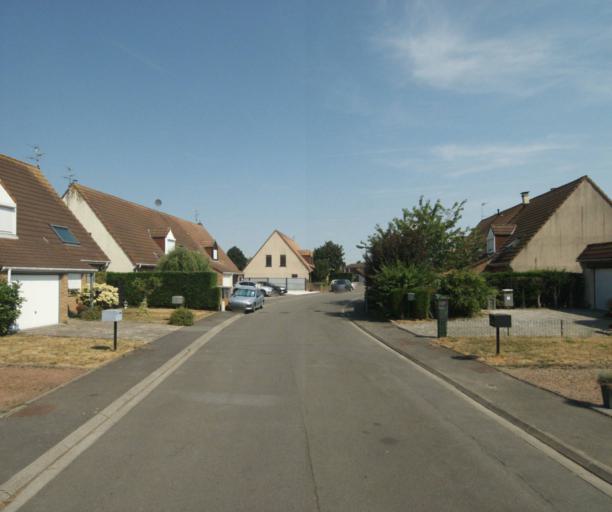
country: FR
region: Nord-Pas-de-Calais
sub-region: Departement du Nord
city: Comines
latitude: 50.7534
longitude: 3.0028
